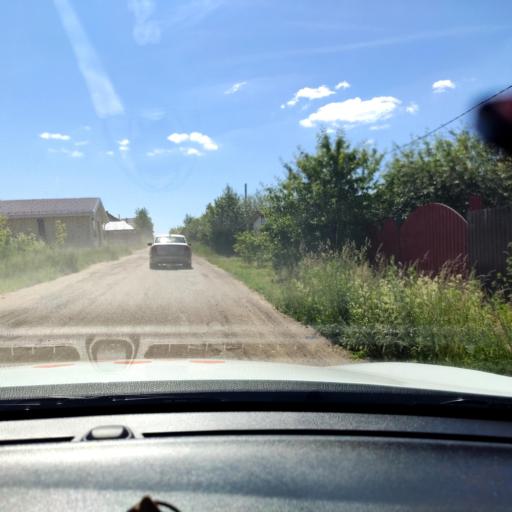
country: RU
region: Tatarstan
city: Vysokaya Gora
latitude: 55.8173
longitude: 49.2855
